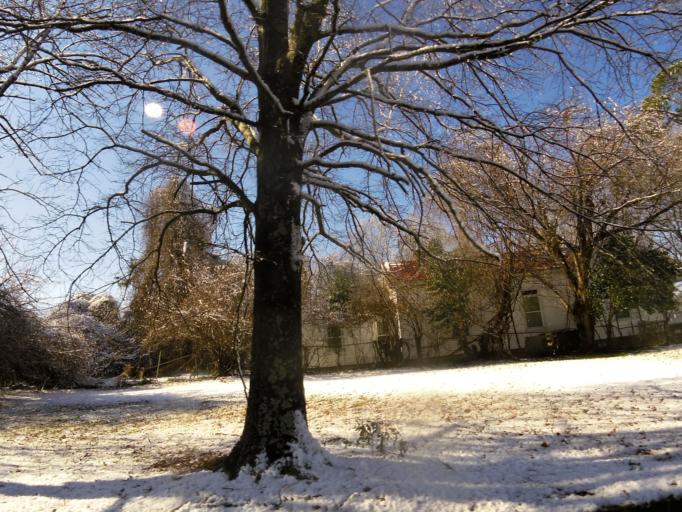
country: US
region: North Carolina
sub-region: Wilson County
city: Wilson
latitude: 35.7289
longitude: -77.9062
